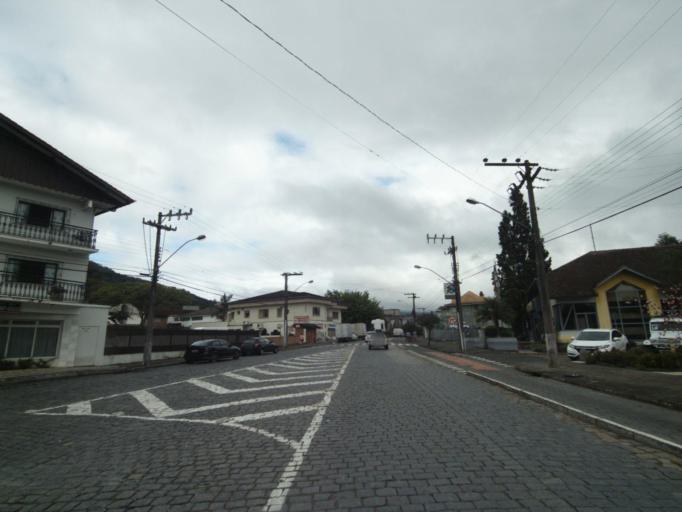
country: BR
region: Santa Catarina
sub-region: Pomerode
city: Pomerode
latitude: -26.7417
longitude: -49.1755
